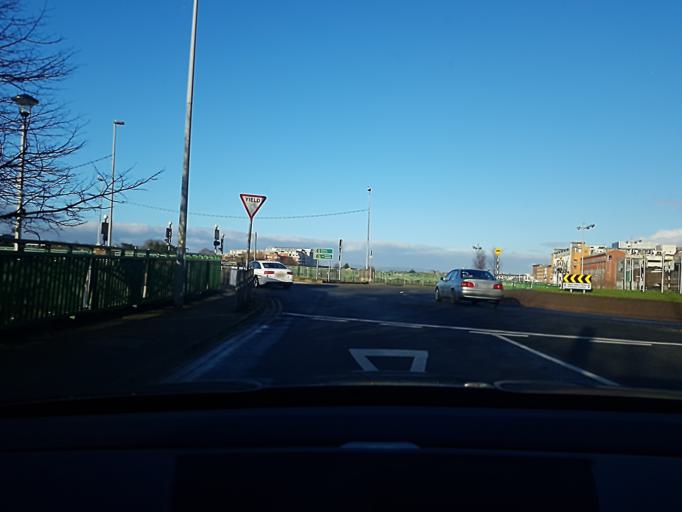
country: IE
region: Munster
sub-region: County Limerick
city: Luimneach
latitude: 52.6611
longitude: -8.6339
